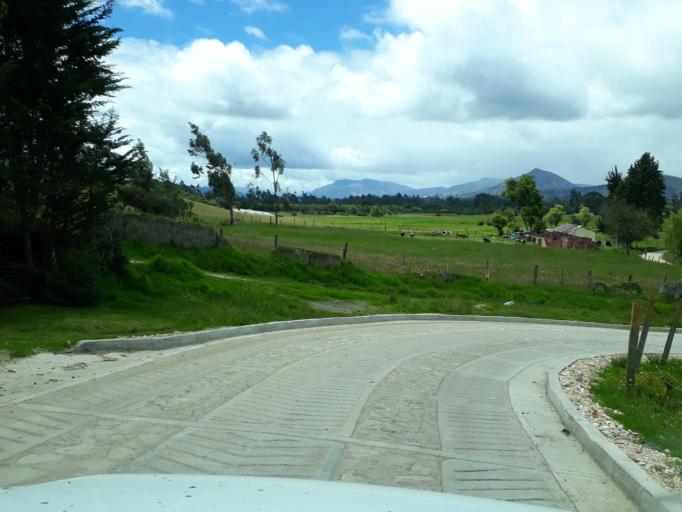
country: CO
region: Cundinamarca
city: Guasca
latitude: 4.8497
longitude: -73.9072
